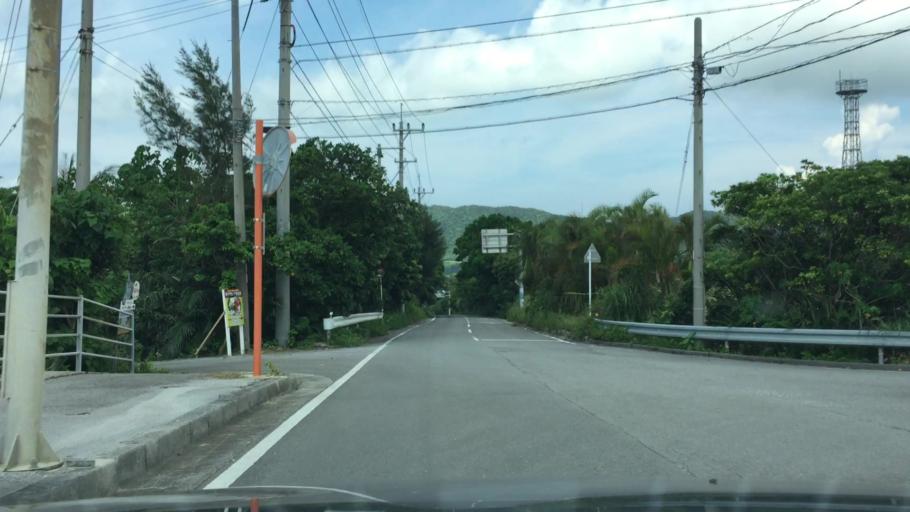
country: JP
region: Okinawa
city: Ishigaki
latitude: 24.4539
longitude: 124.2059
